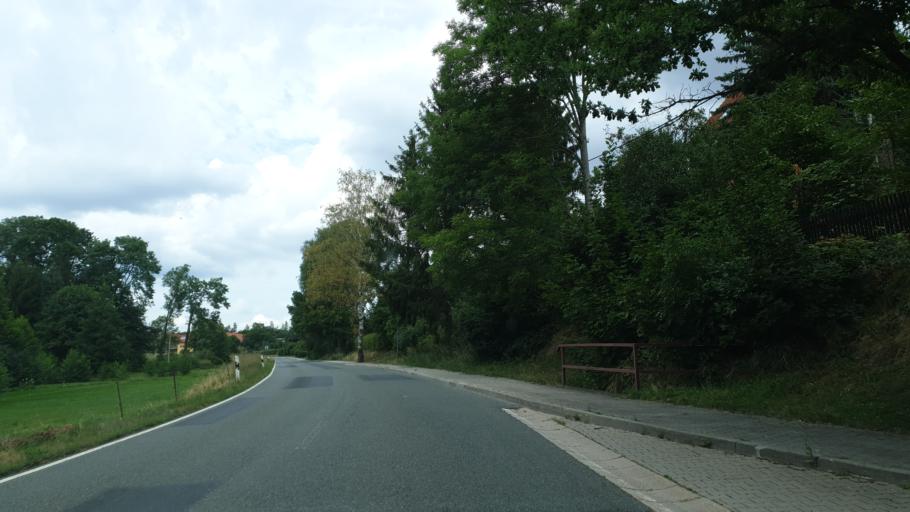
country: DE
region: Saxony
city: Hirschfeld
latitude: 50.6313
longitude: 12.4402
